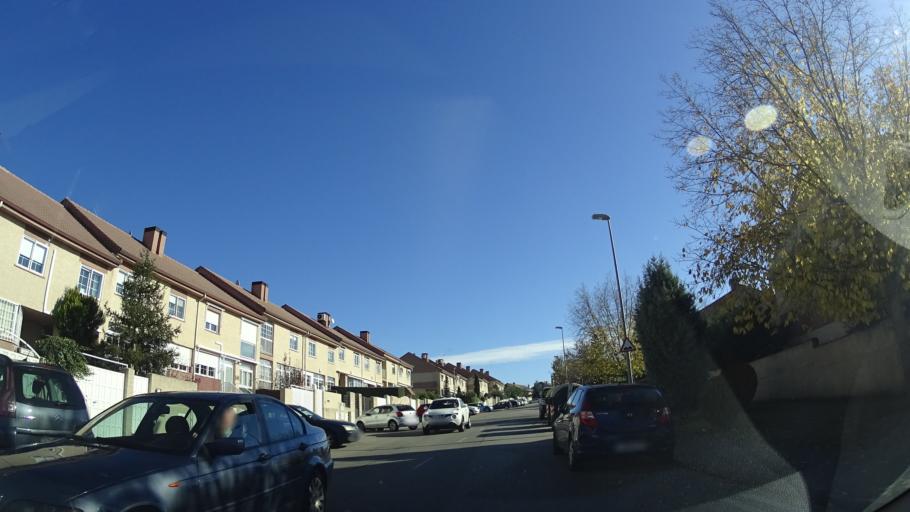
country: ES
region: Madrid
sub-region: Provincia de Madrid
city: Las Matas
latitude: 40.5250
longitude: -3.9152
